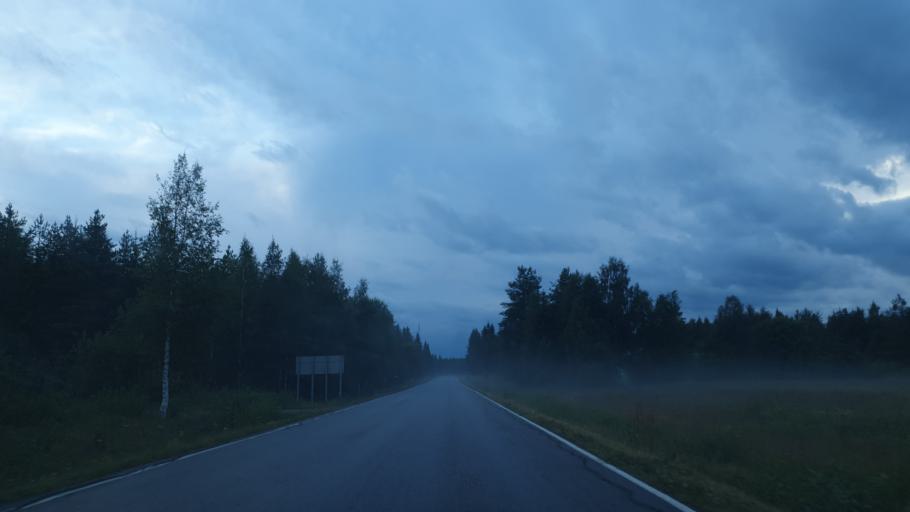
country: FI
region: Kainuu
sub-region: Kehys-Kainuu
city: Kuhmo
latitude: 63.9553
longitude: 29.7146
